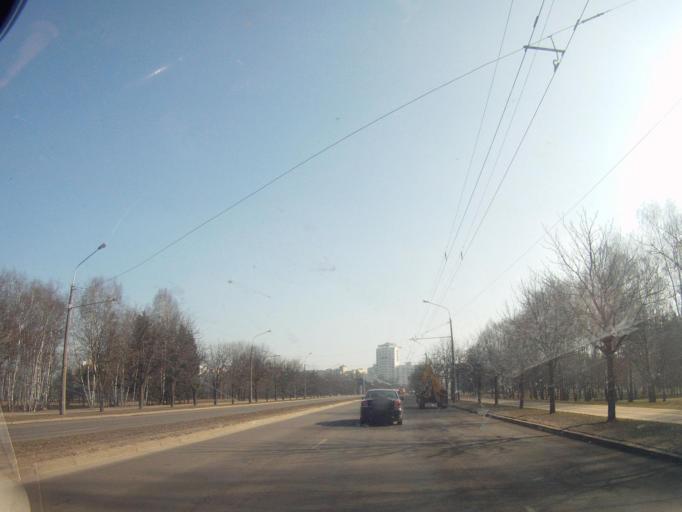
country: BY
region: Minsk
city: Minsk
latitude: 53.9320
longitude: 27.5704
